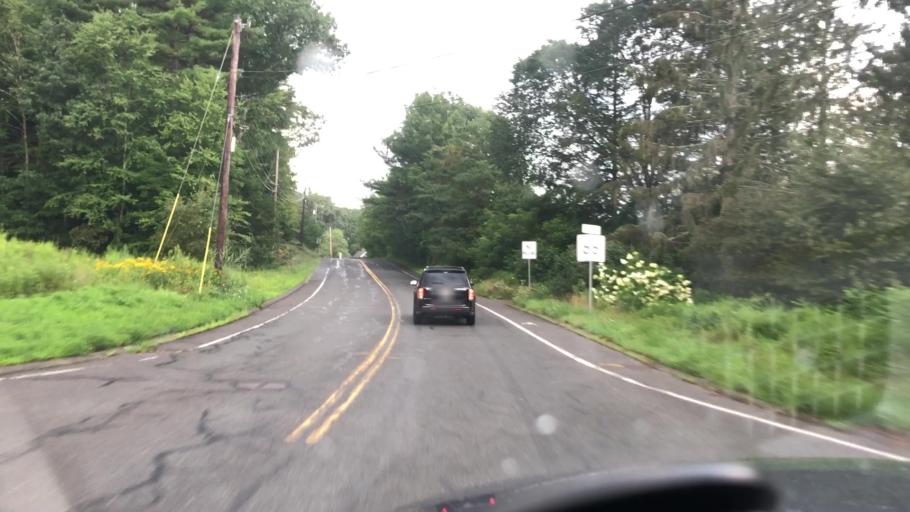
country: US
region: Massachusetts
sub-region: Hampshire County
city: Westhampton
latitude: 42.2939
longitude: -72.7349
